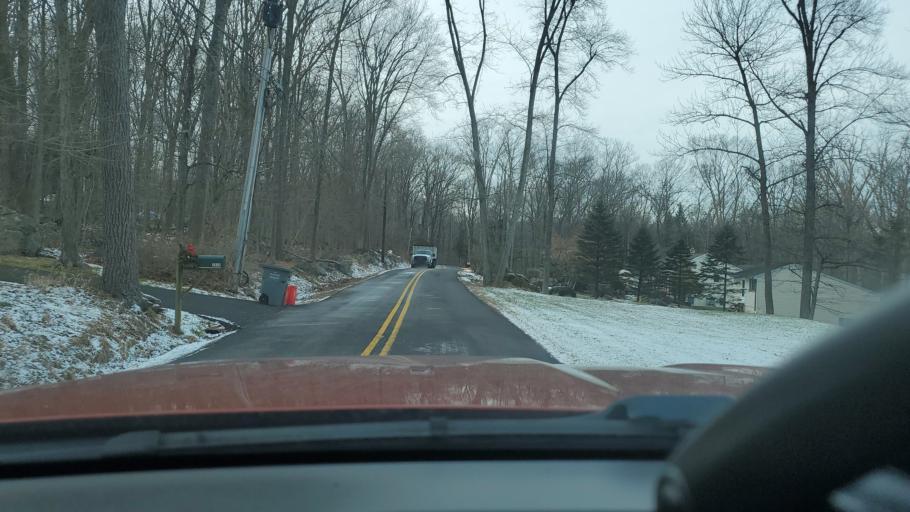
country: US
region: Pennsylvania
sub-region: Montgomery County
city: Red Hill
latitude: 40.3235
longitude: -75.5048
